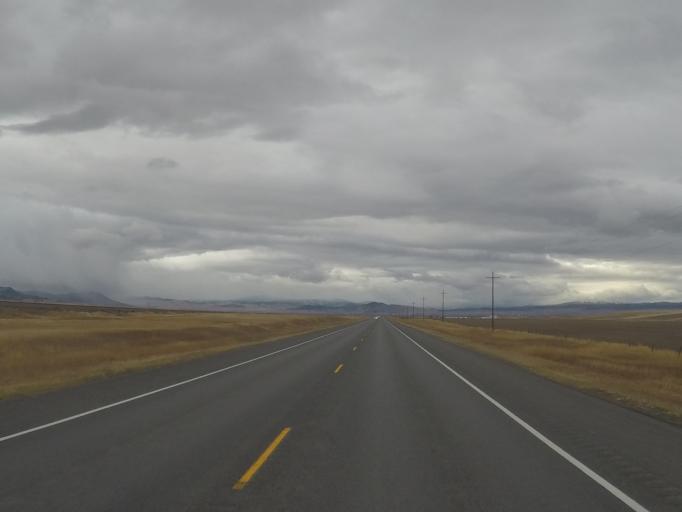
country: US
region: Montana
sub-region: Lewis and Clark County
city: East Helena
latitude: 46.5777
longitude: -111.8396
